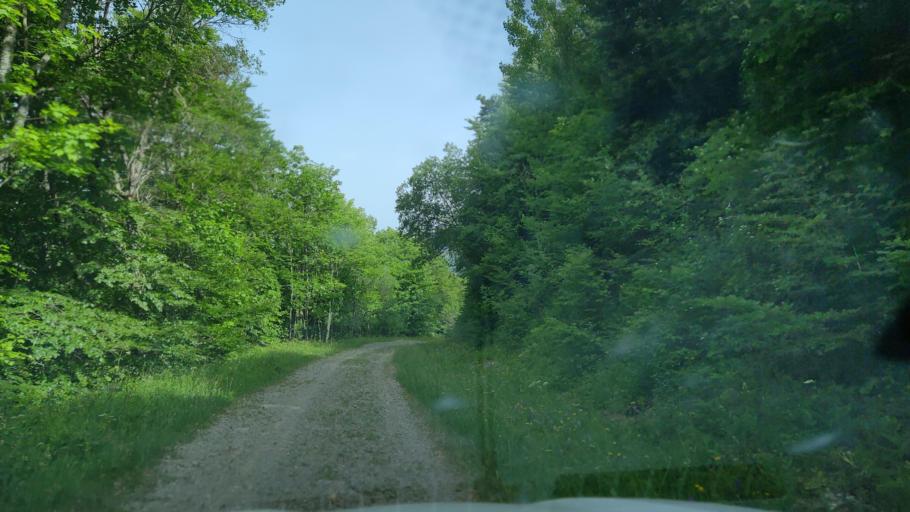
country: FR
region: Rhone-Alpes
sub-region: Departement de la Savoie
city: Cruet
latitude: 45.5886
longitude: 6.1063
